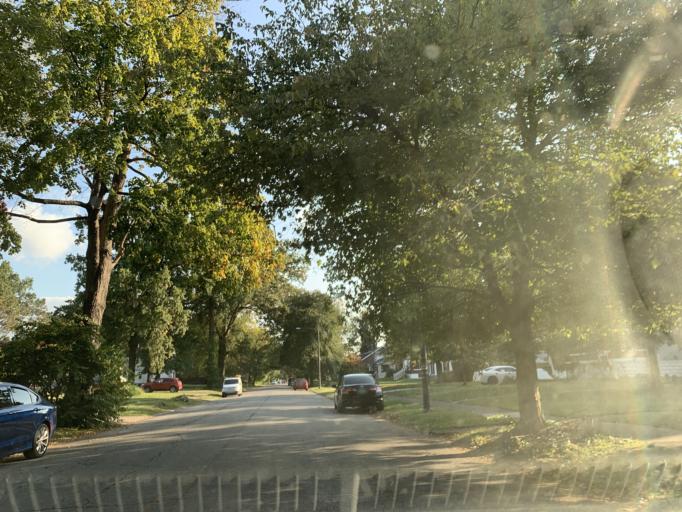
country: US
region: Kentucky
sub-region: Jefferson County
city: Audubon Park
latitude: 38.1862
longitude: -85.7638
